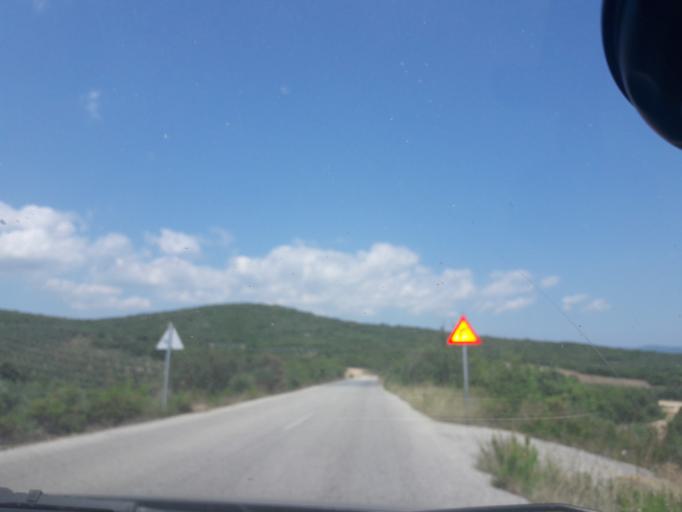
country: GR
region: Central Macedonia
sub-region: Nomos Chalkidikis
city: Ormylia
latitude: 40.3557
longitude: 23.5895
